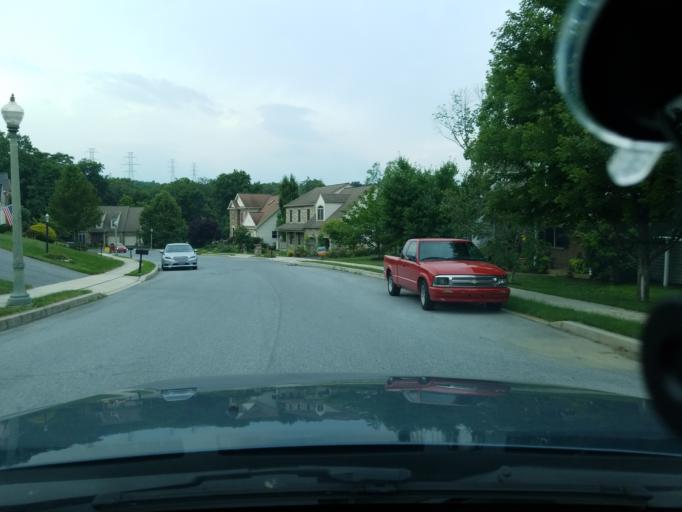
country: US
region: Pennsylvania
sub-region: Dauphin County
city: Hummelstown
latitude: 40.2716
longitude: -76.7263
